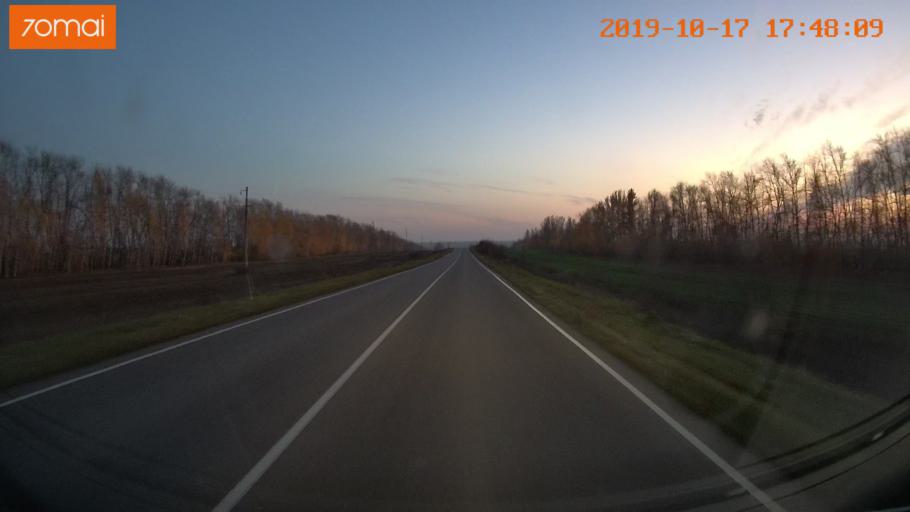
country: RU
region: Tula
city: Yepifan'
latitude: 53.6966
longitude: 38.6962
